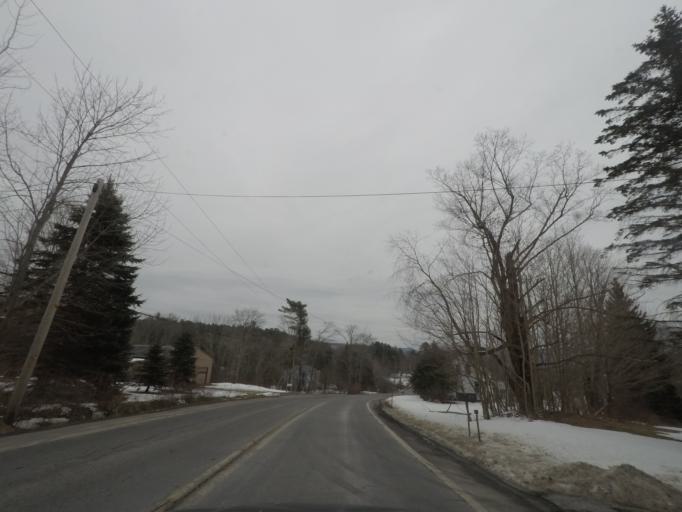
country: US
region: Massachusetts
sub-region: Berkshire County
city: Lanesborough
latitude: 42.5529
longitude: -73.3911
